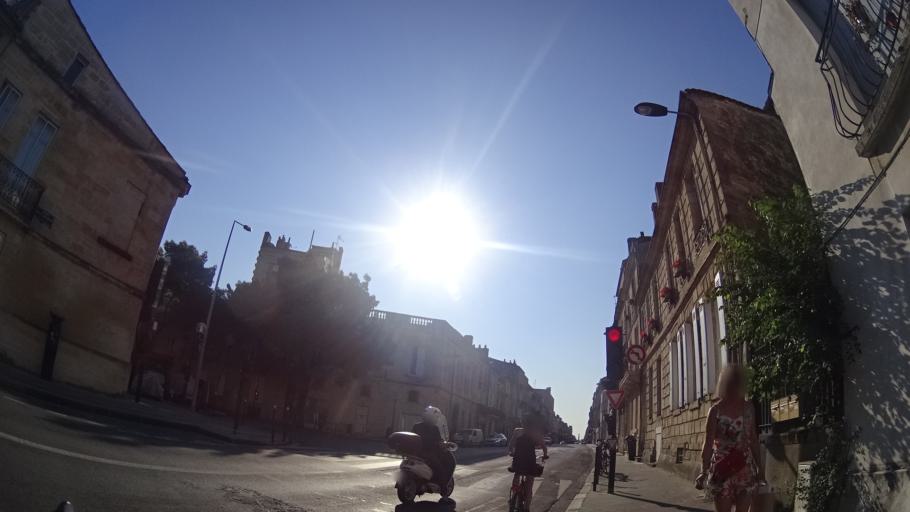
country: FR
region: Aquitaine
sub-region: Departement de la Gironde
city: Bordeaux
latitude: 44.8325
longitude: -0.5800
